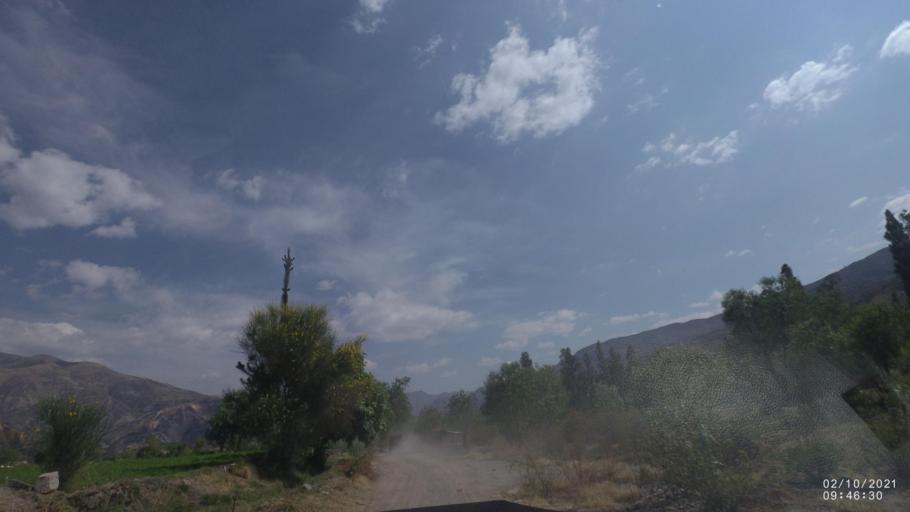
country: BO
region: Cochabamba
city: Irpa Irpa
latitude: -17.8052
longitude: -66.3343
